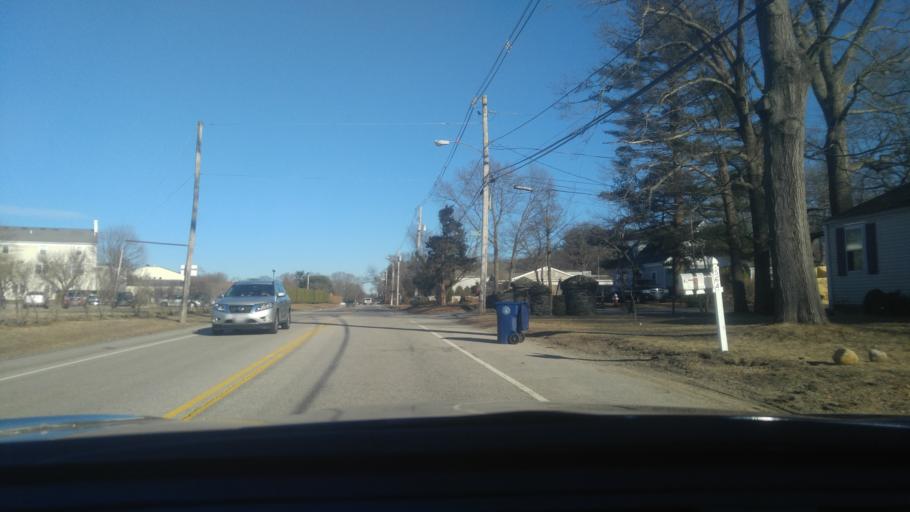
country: US
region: Rhode Island
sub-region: Kent County
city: Warwick
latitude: 41.6986
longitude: -71.4491
